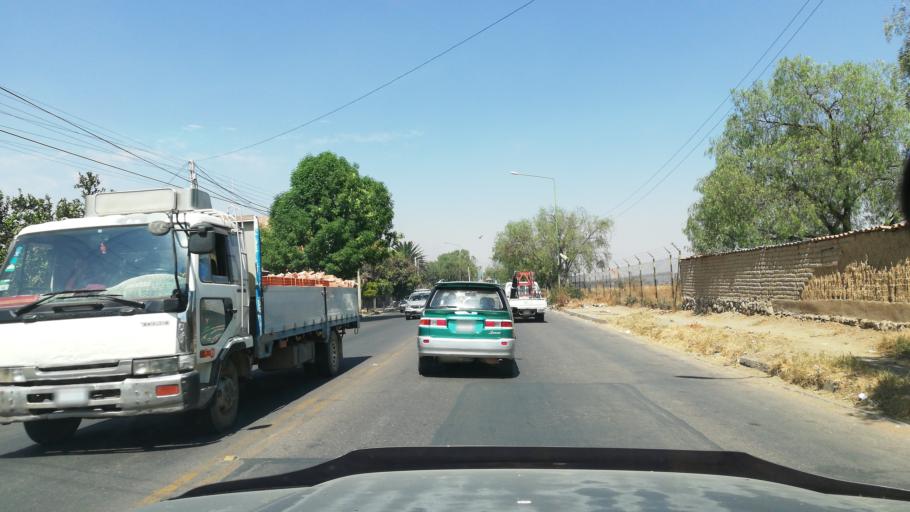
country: BO
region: Cochabamba
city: Cochabamba
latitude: -17.4123
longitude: -66.1680
